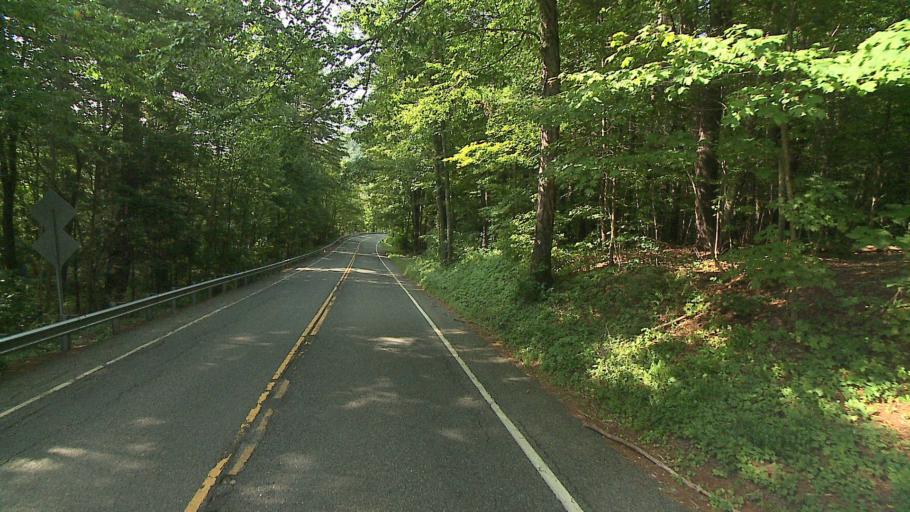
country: US
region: Connecticut
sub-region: Litchfield County
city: Kent
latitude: 41.8346
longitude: -73.3830
